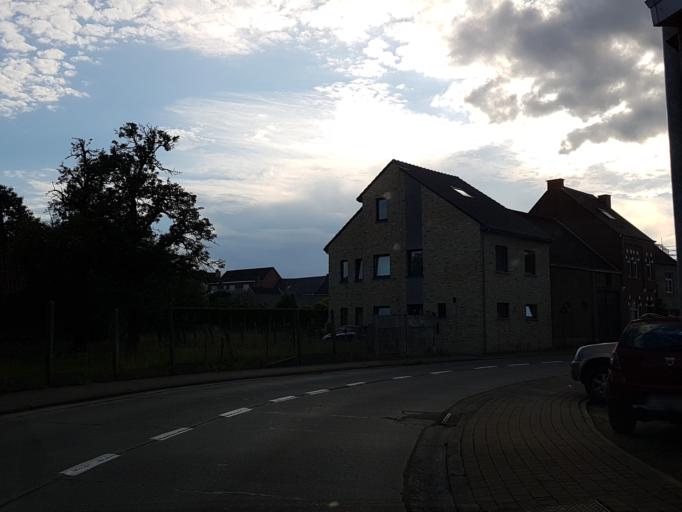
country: BE
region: Flanders
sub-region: Provincie Oost-Vlaanderen
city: Denderleeuw
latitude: 50.9019
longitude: 4.0487
